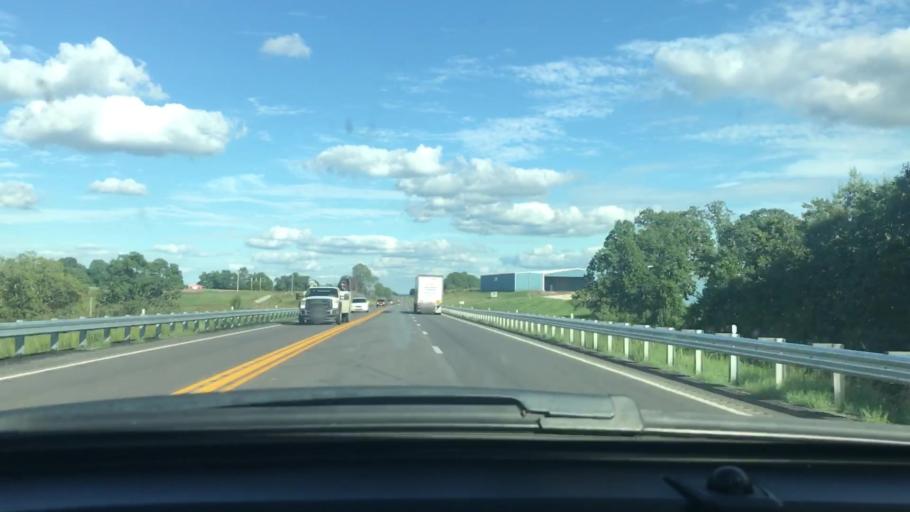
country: US
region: Missouri
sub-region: Oregon County
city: Thayer
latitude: 36.5884
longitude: -91.6364
